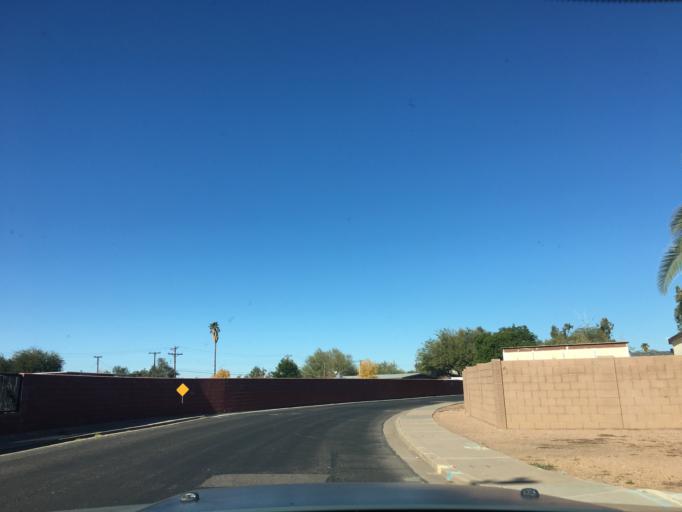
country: US
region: Arizona
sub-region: Maricopa County
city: Mesa
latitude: 33.4450
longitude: -111.8467
